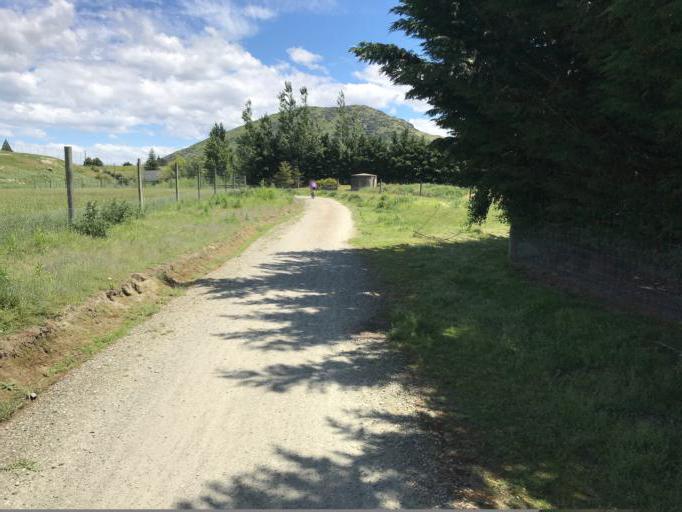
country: NZ
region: Otago
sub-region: Queenstown-Lakes District
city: Arrowtown
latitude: -44.9927
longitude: 168.8595
